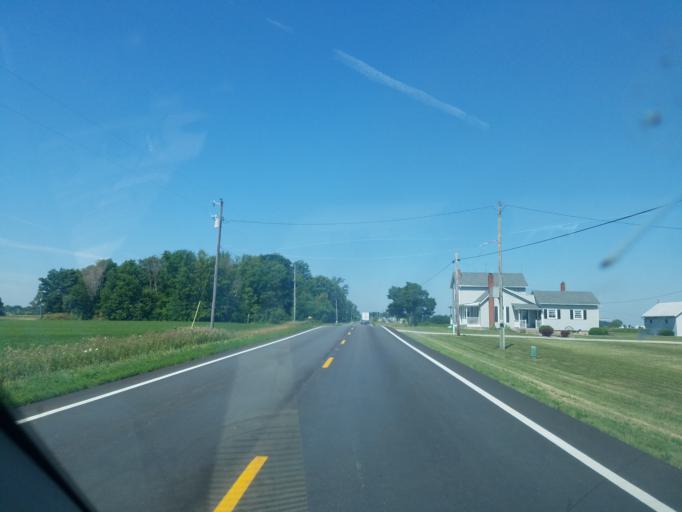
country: US
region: Ohio
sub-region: Shelby County
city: Jackson Center
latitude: 40.4396
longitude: -84.0813
